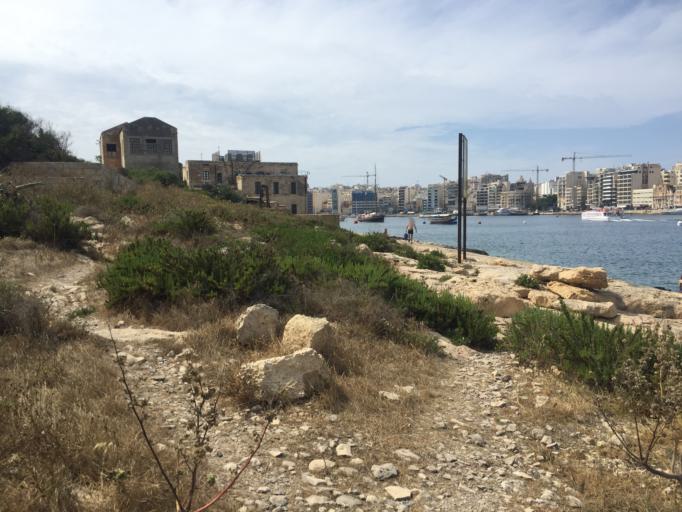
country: MT
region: Il-Furjana
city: Floriana
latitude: 35.9039
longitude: 14.5073
